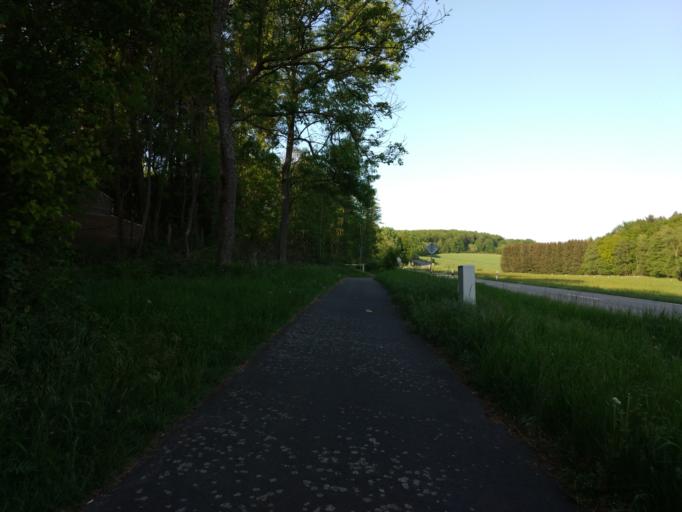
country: DE
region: Saarland
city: Saarwellingen
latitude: 49.3642
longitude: 6.8236
